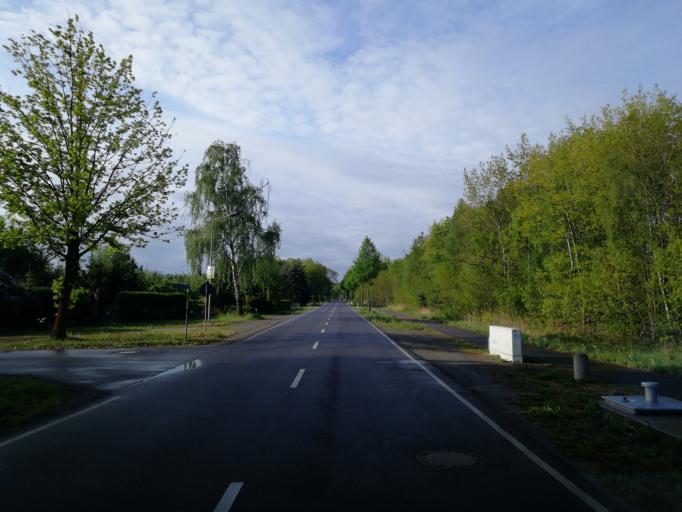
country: DE
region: Brandenburg
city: Lauchhammer
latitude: 51.5133
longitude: 13.7490
